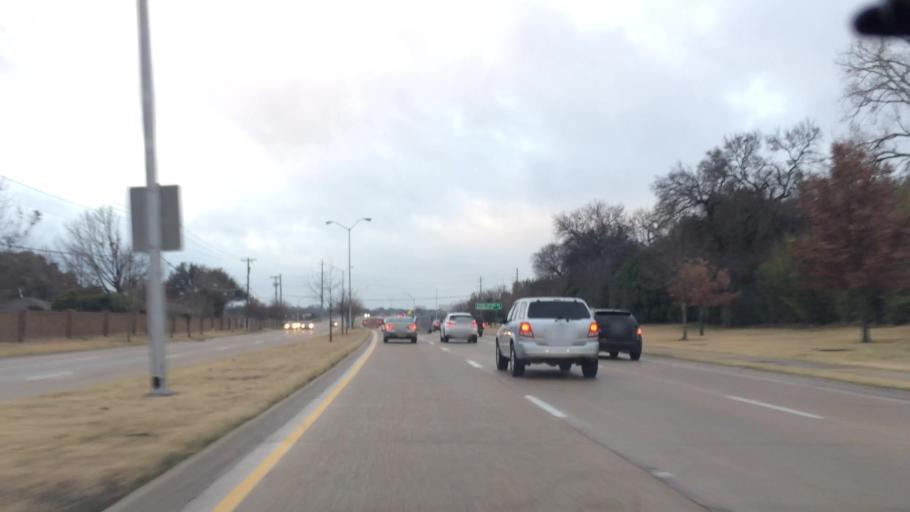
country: US
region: Texas
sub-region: Dallas County
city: Addison
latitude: 32.9749
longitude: -96.8040
